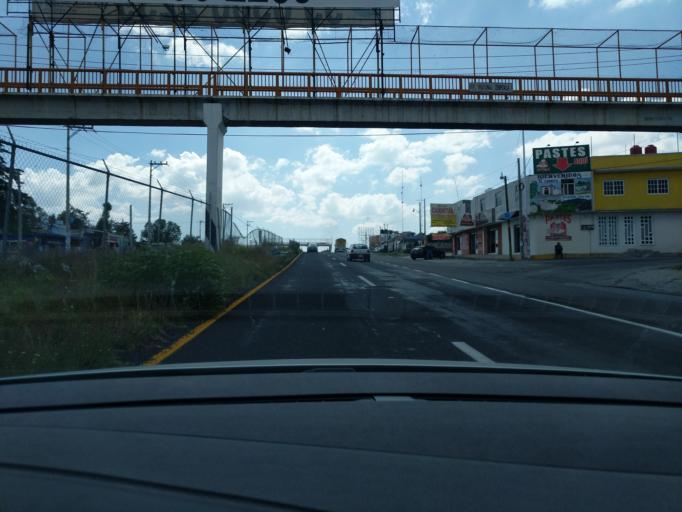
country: MX
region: Hidalgo
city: Zempoala
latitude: 19.9183
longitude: -98.6791
